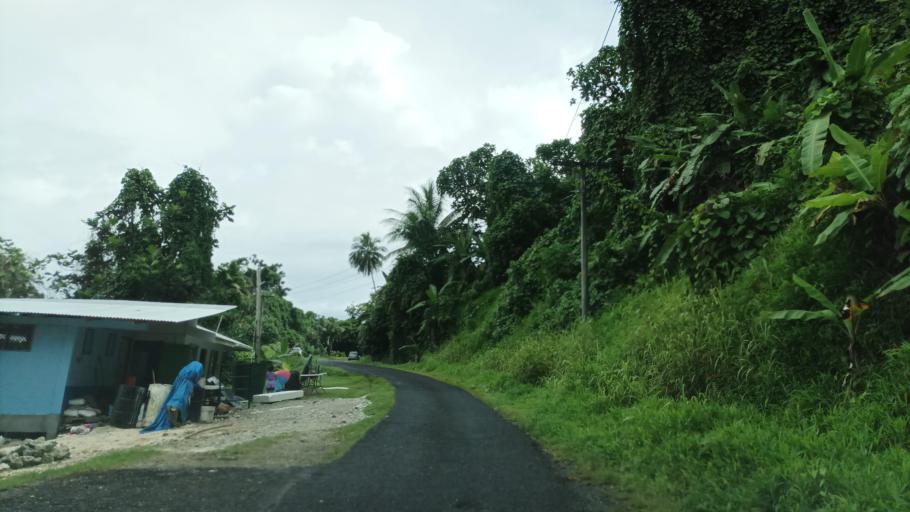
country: FM
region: Pohnpei
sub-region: Madolenihm Municipality
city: Madolenihm Municipality Government
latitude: 6.9184
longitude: 158.3070
